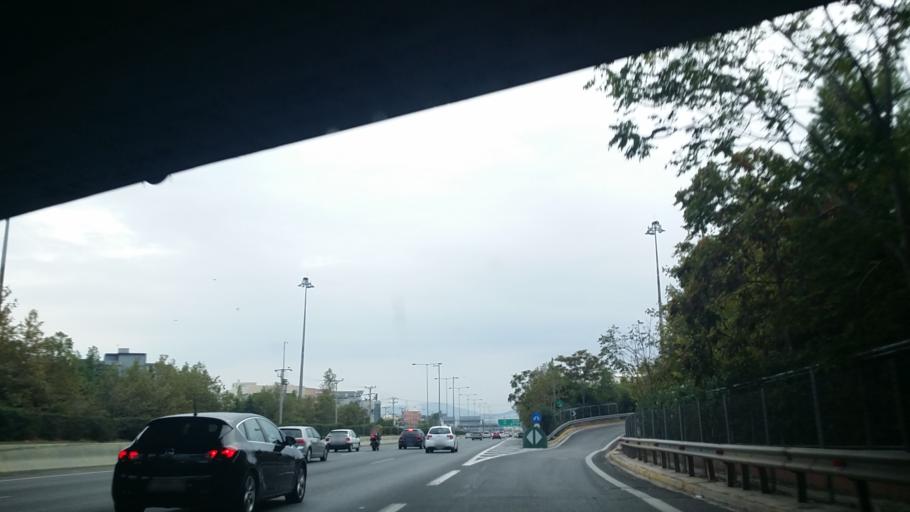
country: GR
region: Attica
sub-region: Nomarchia Athinas
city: Metamorfosi
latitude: 38.0689
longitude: 23.7601
